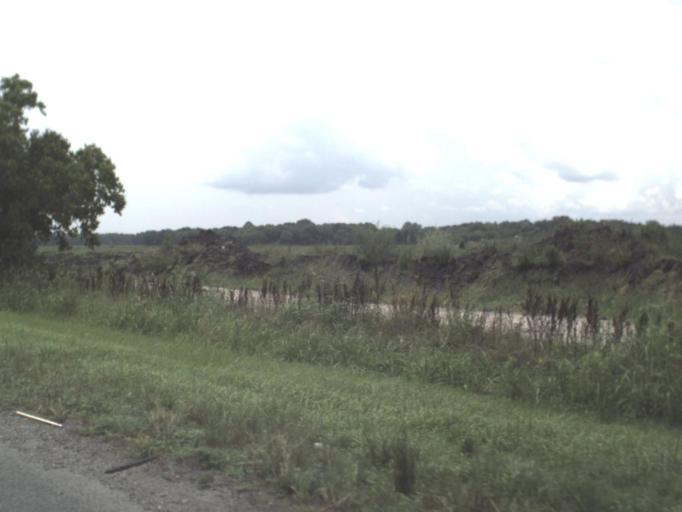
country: US
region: Florida
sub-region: Nassau County
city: Callahan
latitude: 30.6168
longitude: -81.8424
